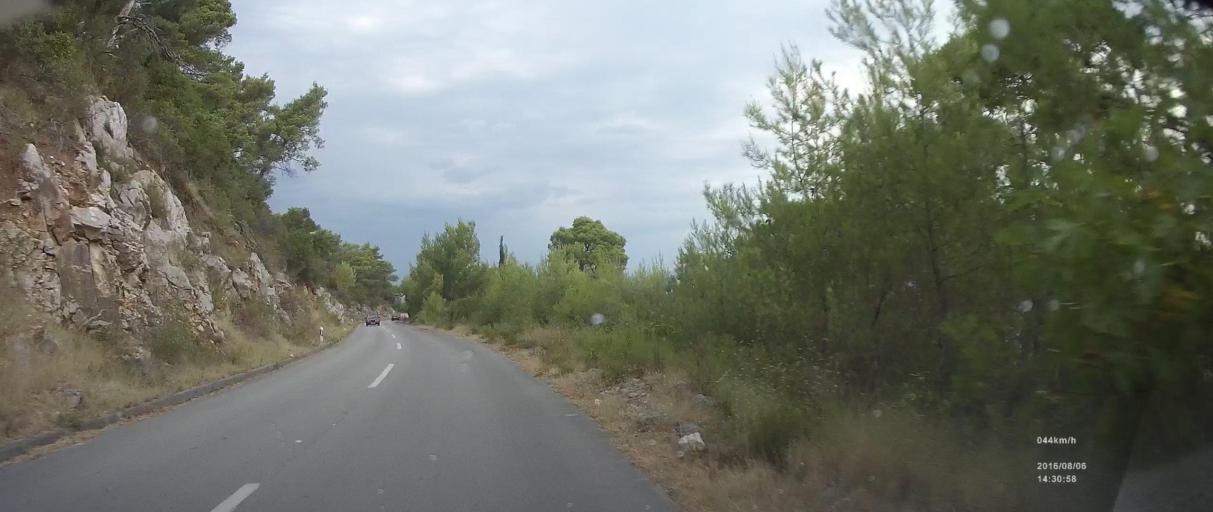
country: HR
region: Dubrovacko-Neretvanska
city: Ston
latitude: 42.7117
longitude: 17.7236
